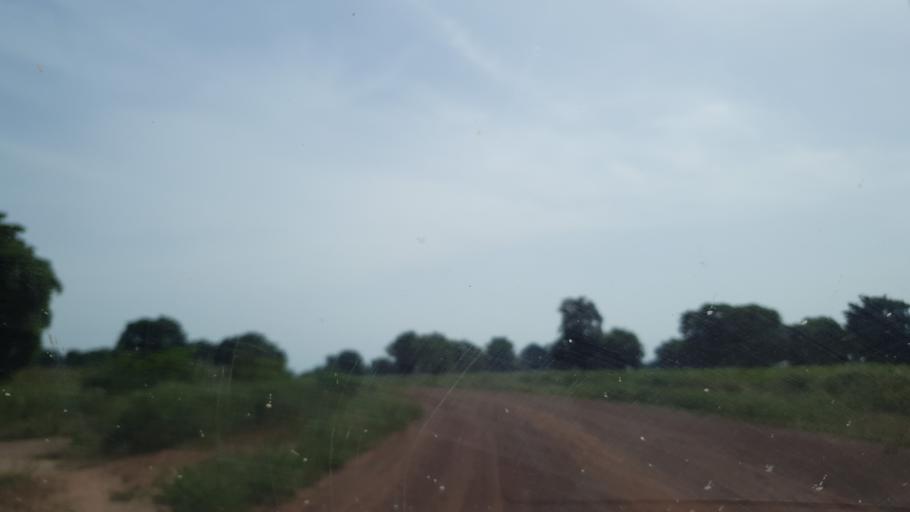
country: ML
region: Koulikoro
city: Dioila
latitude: 12.4117
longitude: -6.2500
